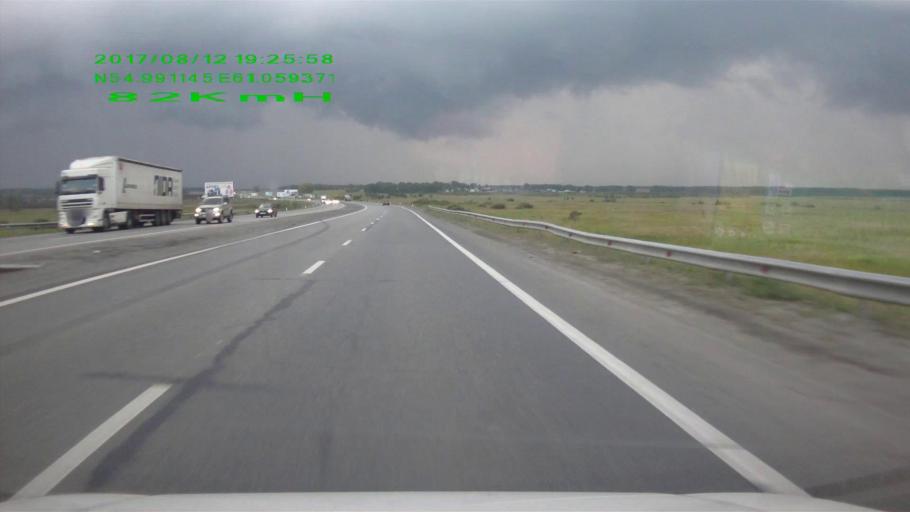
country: RU
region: Chelyabinsk
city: Poletayevo
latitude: 54.9909
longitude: 61.0559
